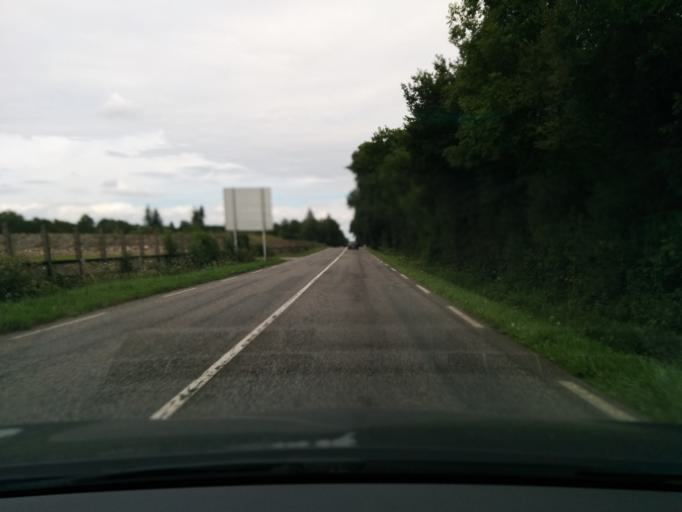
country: FR
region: Midi-Pyrenees
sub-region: Departement des Hautes-Pyrenees
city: La Barthe-de-Neste
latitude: 43.0934
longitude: 0.3917
